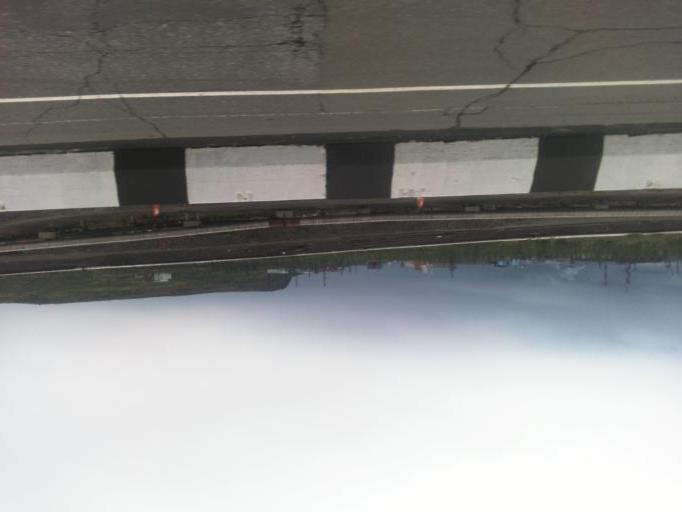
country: RU
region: Krasnoyarskiy
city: Norilsk
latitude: 69.3605
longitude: 88.0451
